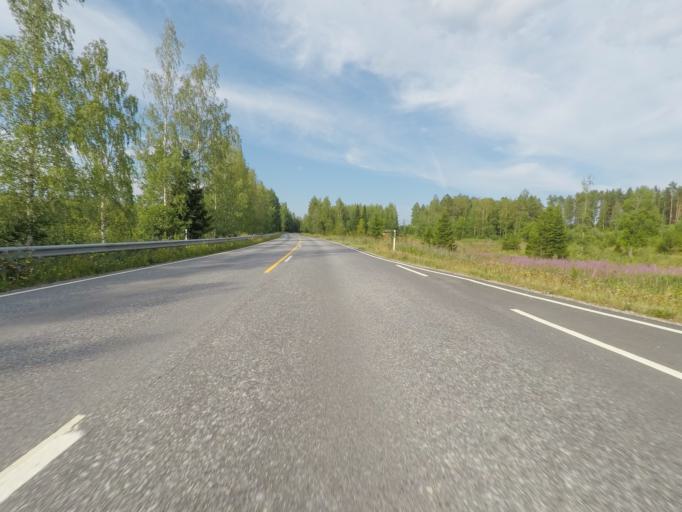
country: FI
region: Southern Savonia
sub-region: Savonlinna
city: Sulkava
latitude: 61.9013
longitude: 28.5838
